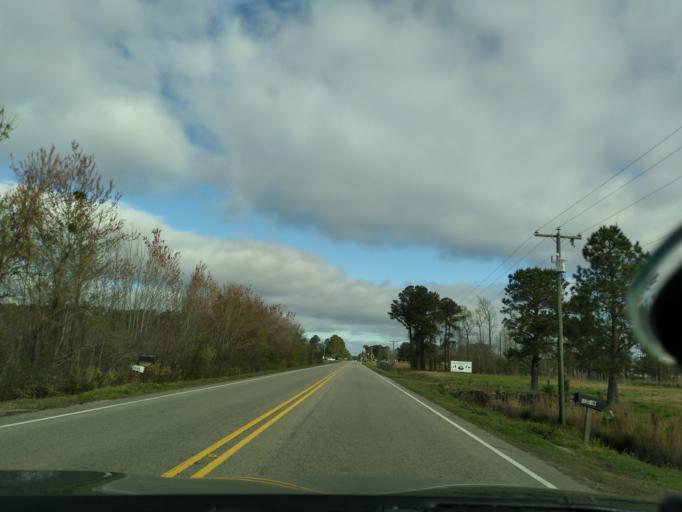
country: US
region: North Carolina
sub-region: Washington County
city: Plymouth
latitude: 35.8889
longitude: -76.7005
